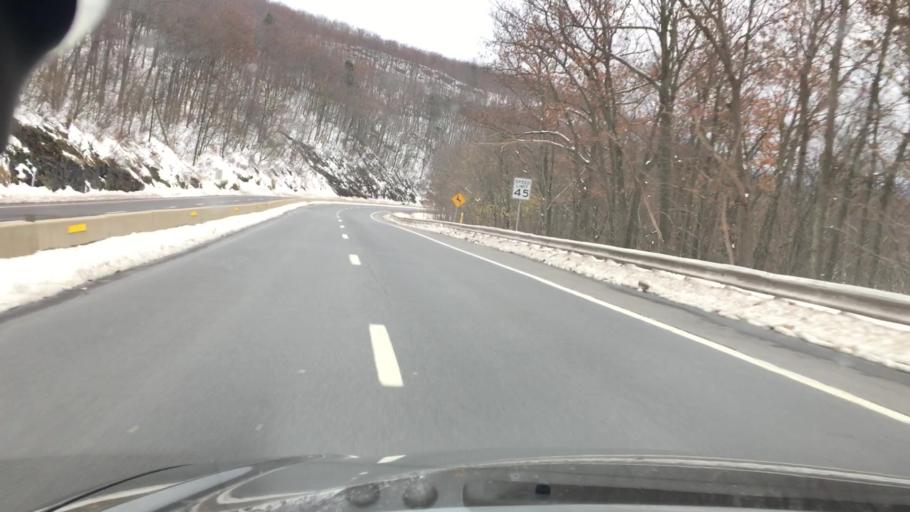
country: US
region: Pennsylvania
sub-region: Luzerne County
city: Mountain Top
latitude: 41.1803
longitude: -75.8866
